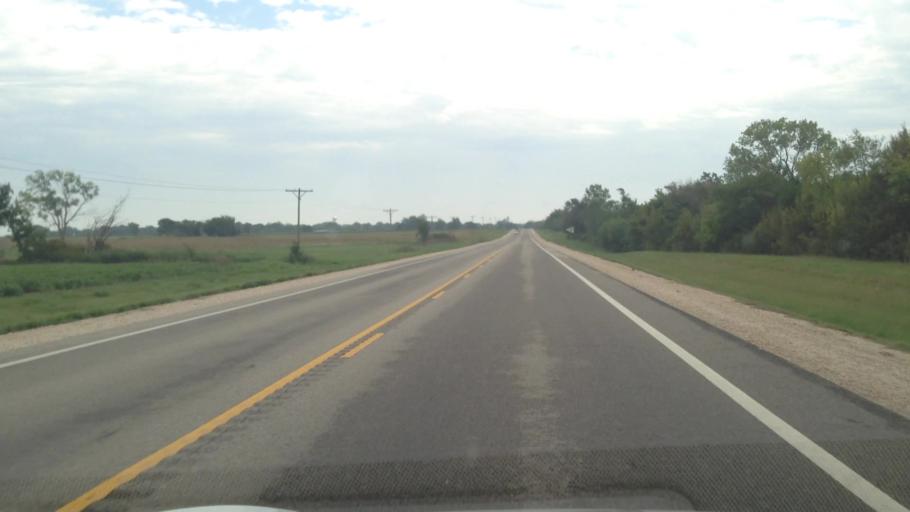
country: US
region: Kansas
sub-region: Allen County
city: Iola
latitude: 37.9035
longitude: -95.0903
